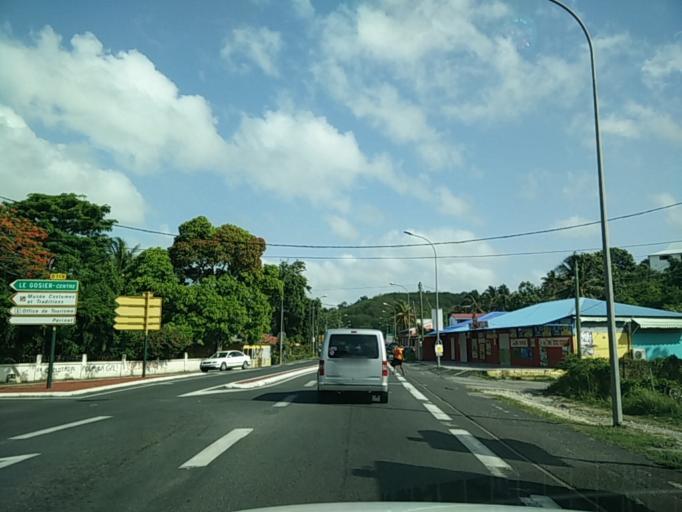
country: GP
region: Guadeloupe
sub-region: Guadeloupe
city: Le Gosier
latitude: 16.2135
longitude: -61.4775
